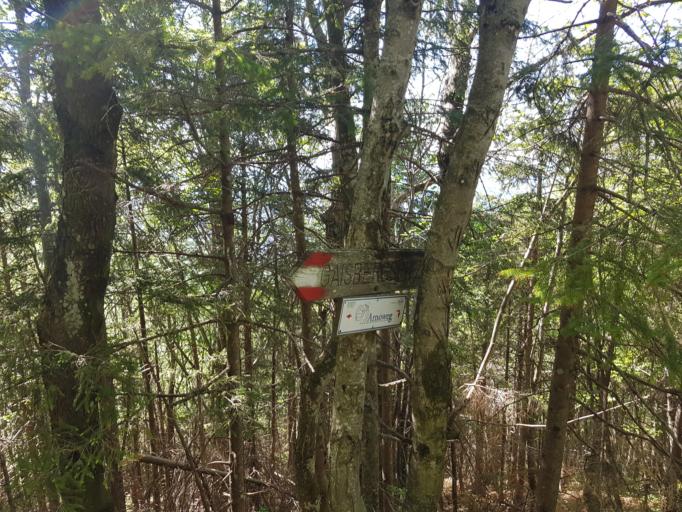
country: AT
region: Salzburg
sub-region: Politischer Bezirk Salzburg-Umgebung
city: Koppl
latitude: 47.8072
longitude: 13.1085
